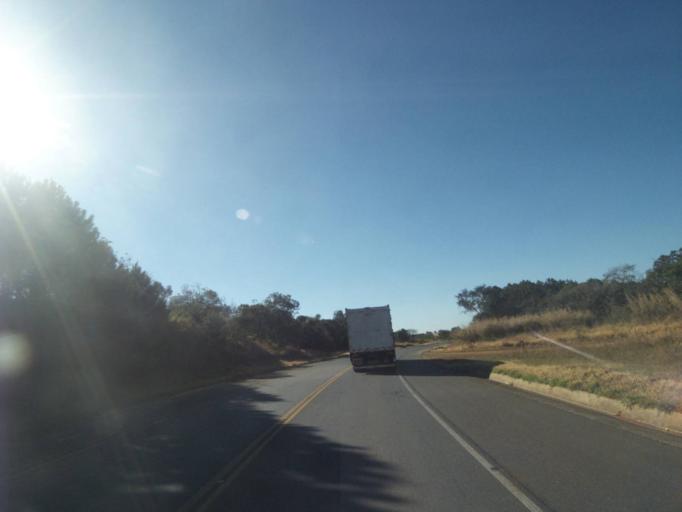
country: BR
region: Parana
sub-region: Tibagi
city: Tibagi
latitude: -24.5289
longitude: -50.4478
